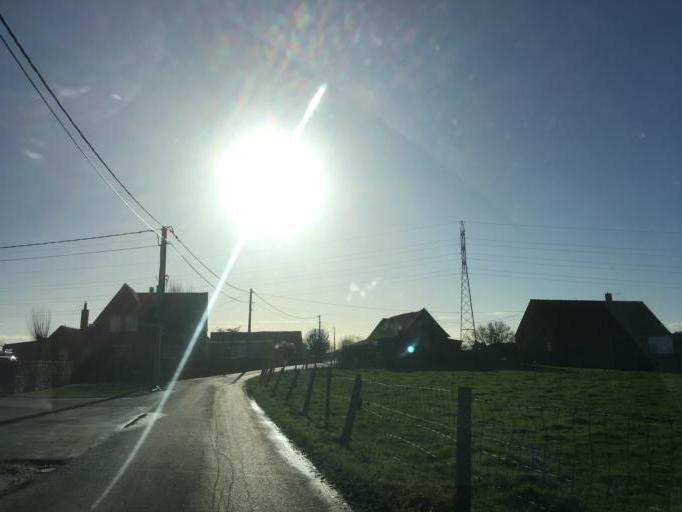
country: BE
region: Flanders
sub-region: Provincie West-Vlaanderen
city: Ardooie
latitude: 50.9643
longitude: 3.1597
